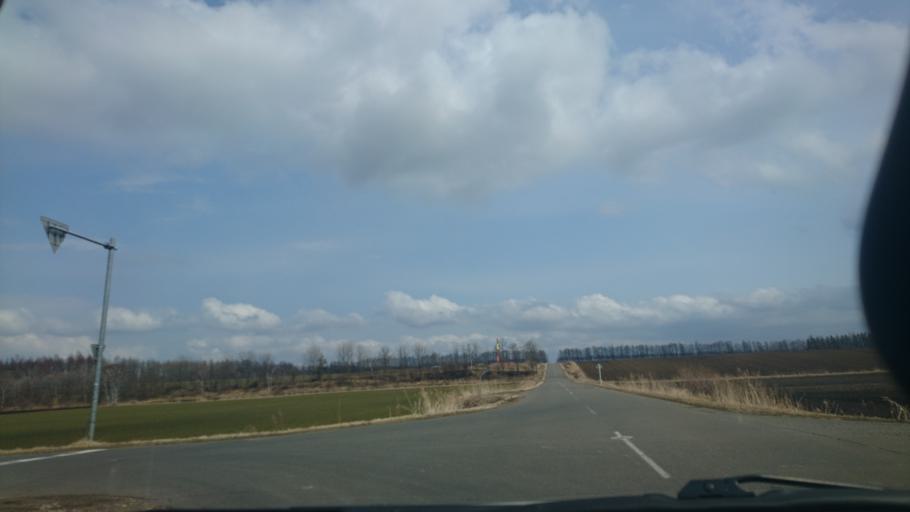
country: JP
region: Hokkaido
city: Otofuke
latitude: 43.2055
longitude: 143.2885
